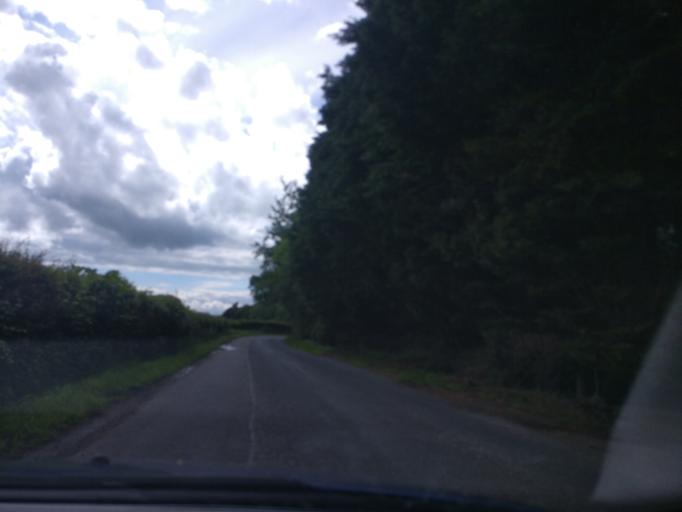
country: GB
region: Scotland
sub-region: East Lothian
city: Haddington
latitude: 55.8844
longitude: -2.7403
